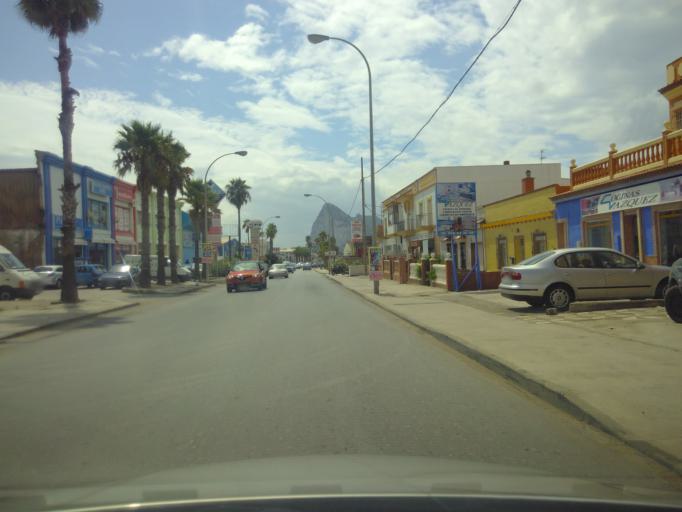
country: ES
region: Andalusia
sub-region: Provincia de Cadiz
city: La Linea de la Concepcion
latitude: 36.1812
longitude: -5.3495
